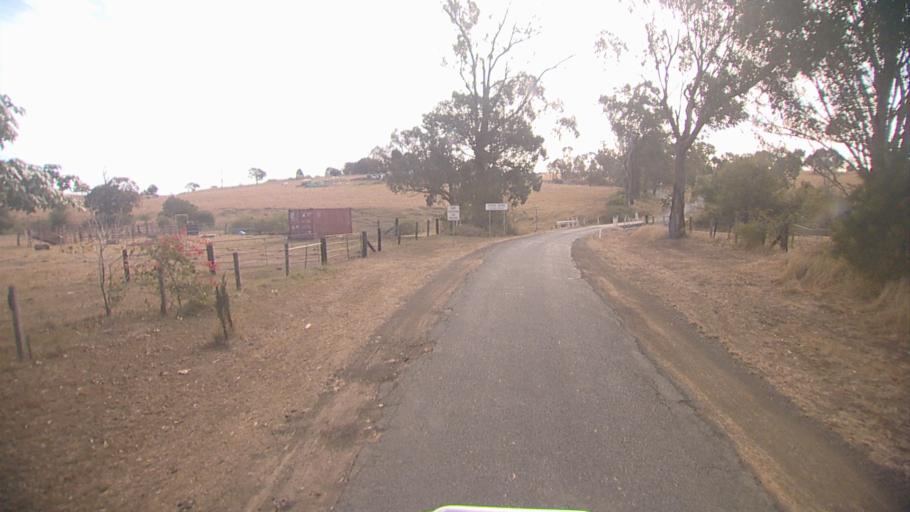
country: AU
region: Queensland
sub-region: Logan
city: Cedar Vale
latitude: -27.9179
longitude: 153.0009
